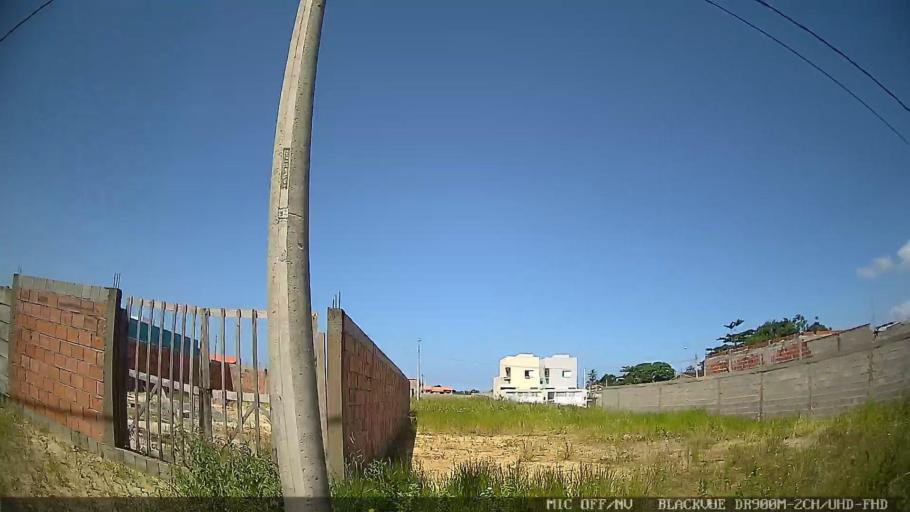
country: BR
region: Sao Paulo
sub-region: Peruibe
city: Peruibe
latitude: -24.2978
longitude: -47.0028
